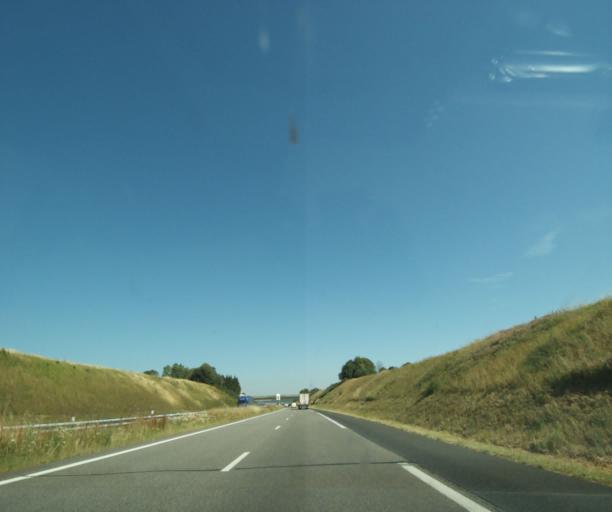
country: FR
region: Lorraine
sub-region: Departement des Vosges
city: Chatenois
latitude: 48.2653
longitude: 5.8634
